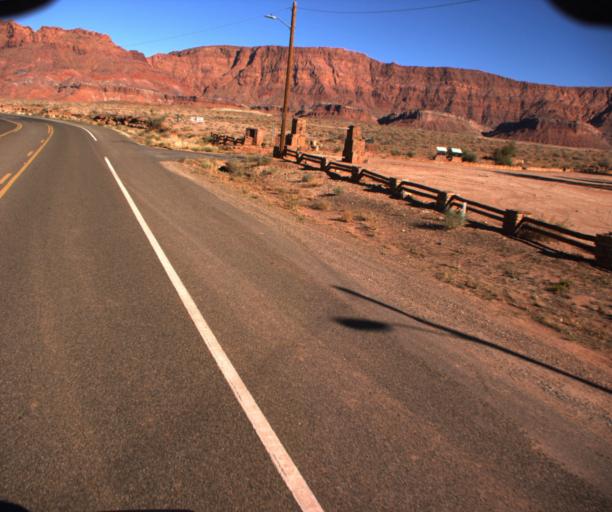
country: US
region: Arizona
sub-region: Coconino County
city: Page
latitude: 36.8163
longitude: -111.6377
